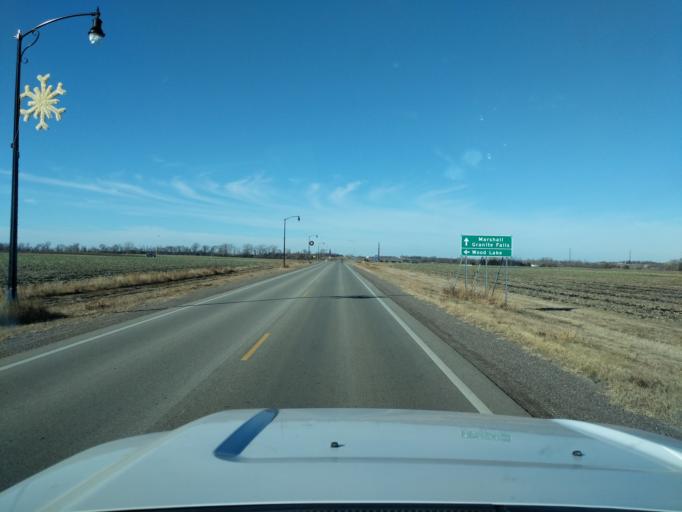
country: US
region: Minnesota
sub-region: Yellow Medicine County
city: Granite Falls
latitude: 44.7689
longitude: -95.5401
